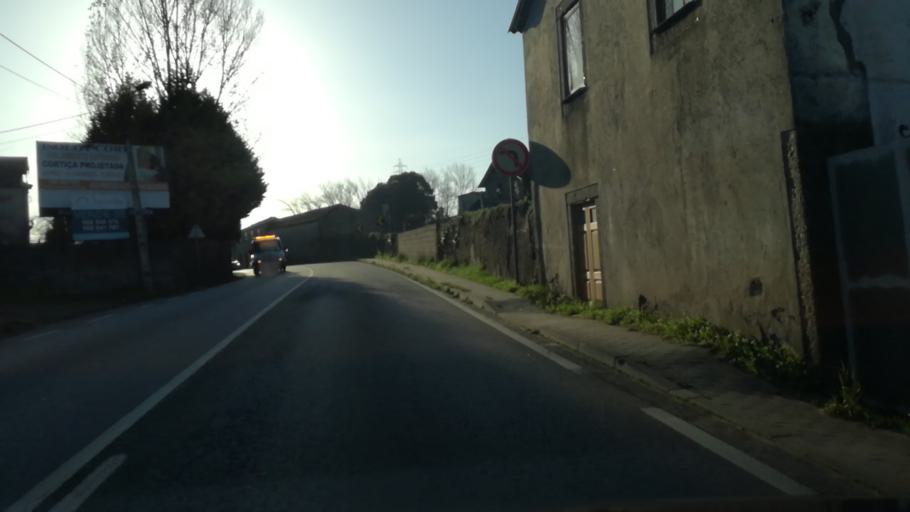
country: PT
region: Braga
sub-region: Vila Nova de Famalicao
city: Ferreiros
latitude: 41.3567
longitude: -8.5514
